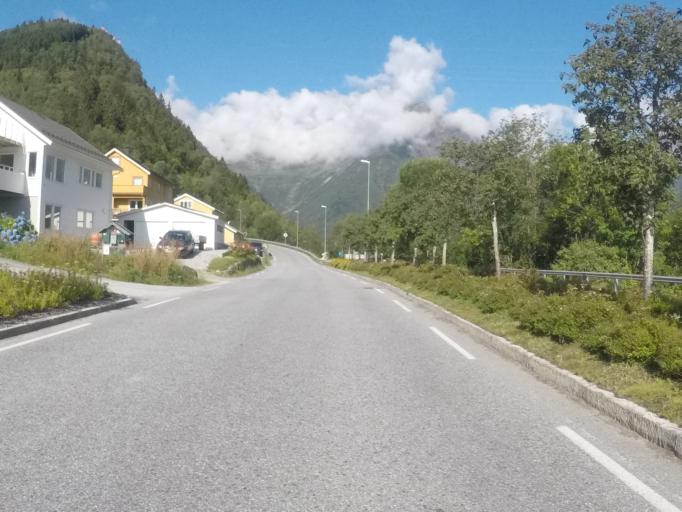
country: NO
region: Sogn og Fjordane
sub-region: Balestrand
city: Balestrand
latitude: 61.2103
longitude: 6.5329
